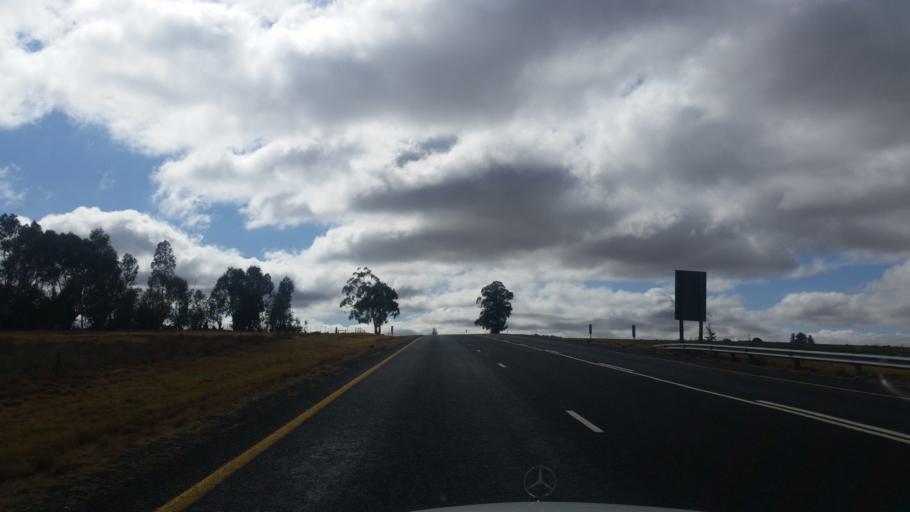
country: ZA
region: Orange Free State
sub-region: Thabo Mofutsanyana District Municipality
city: Phuthaditjhaba
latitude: -28.2959
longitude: 28.8095
